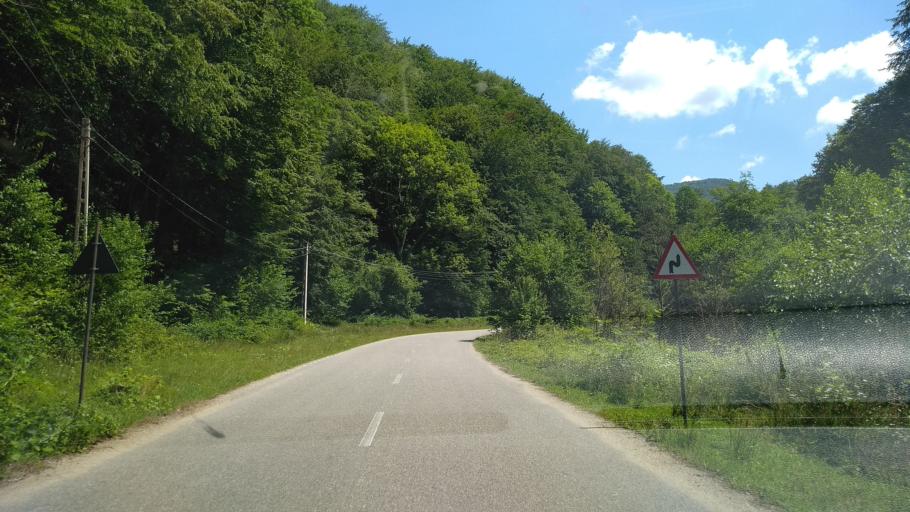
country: RO
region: Hunedoara
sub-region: Comuna Orastioara de Sus
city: Orastioara de Sus
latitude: 45.6299
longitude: 23.2173
